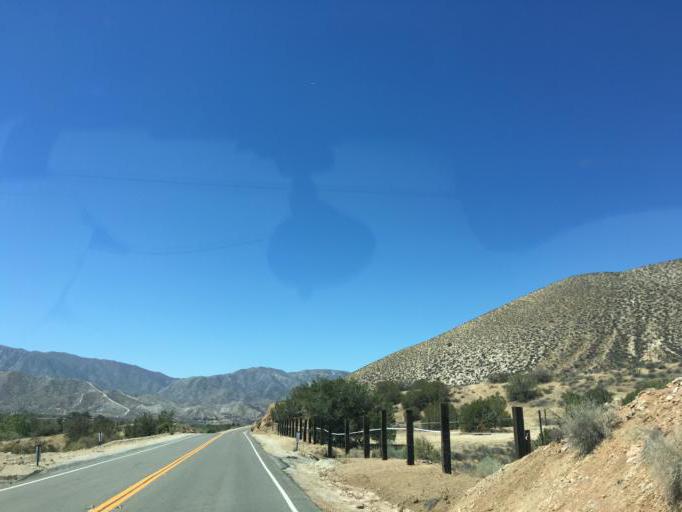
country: US
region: California
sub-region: Los Angeles County
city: Acton
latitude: 34.4532
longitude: -118.2019
